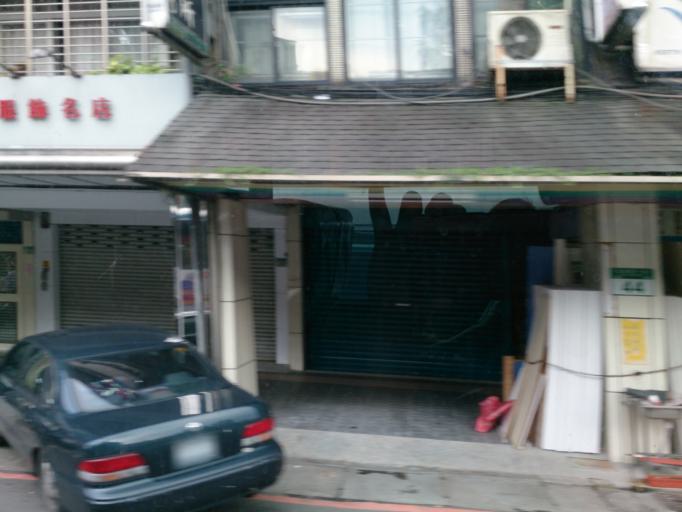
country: TW
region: Taipei
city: Taipei
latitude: 24.9661
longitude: 121.5410
